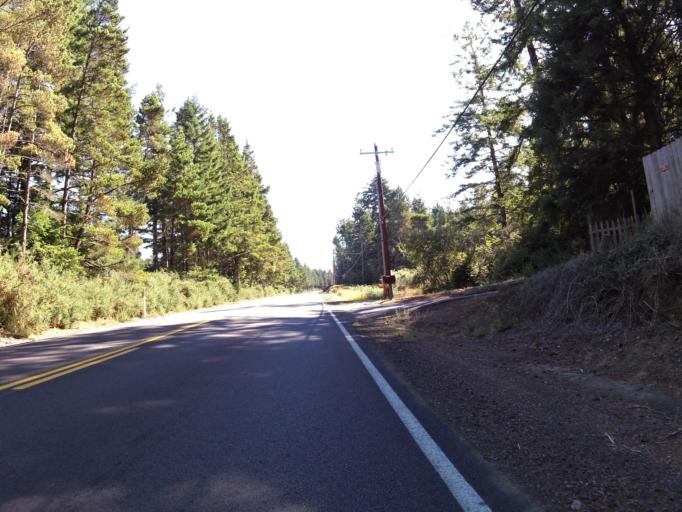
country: US
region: Oregon
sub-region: Coos County
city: Bandon
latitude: 43.2066
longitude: -124.3684
